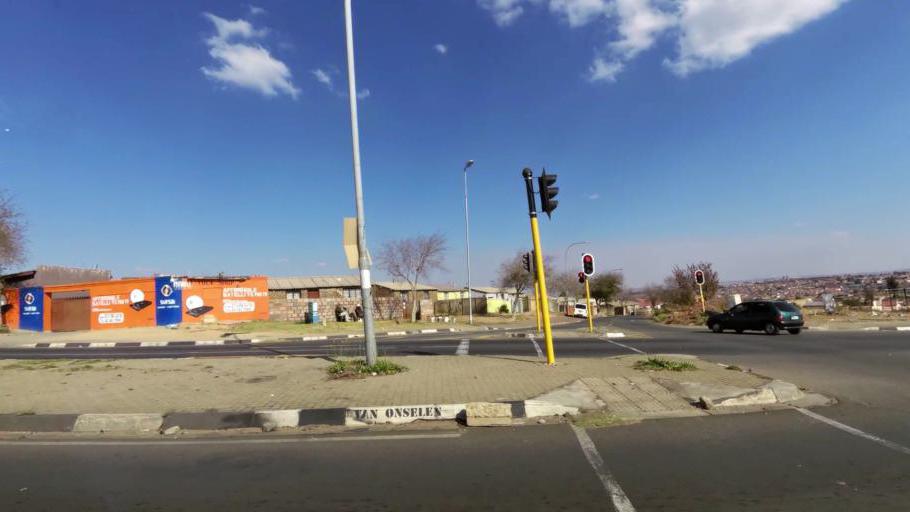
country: ZA
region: Gauteng
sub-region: City of Johannesburg Metropolitan Municipality
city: Roodepoort
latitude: -26.2146
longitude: 27.8866
